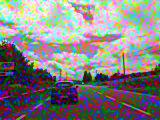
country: IE
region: Ulster
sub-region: County Donegal
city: Letterkenny
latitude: 54.8769
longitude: -7.7433
